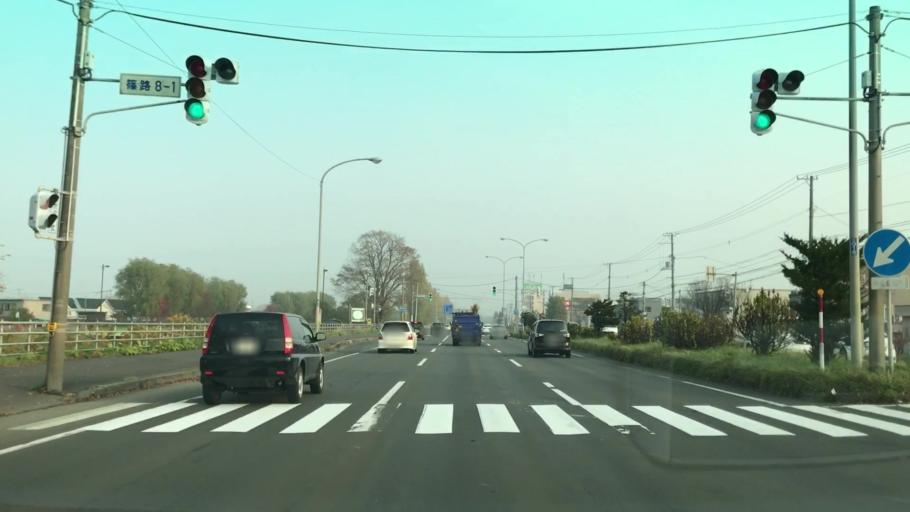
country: JP
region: Hokkaido
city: Ishikari
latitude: 43.1538
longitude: 141.3517
